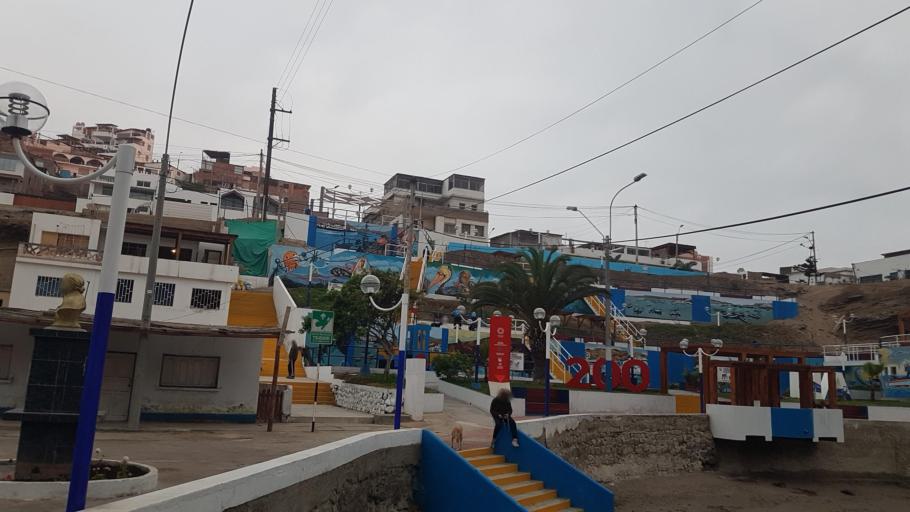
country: PE
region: Lima
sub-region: Lima
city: Pucusana
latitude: -12.4819
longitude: -76.8005
